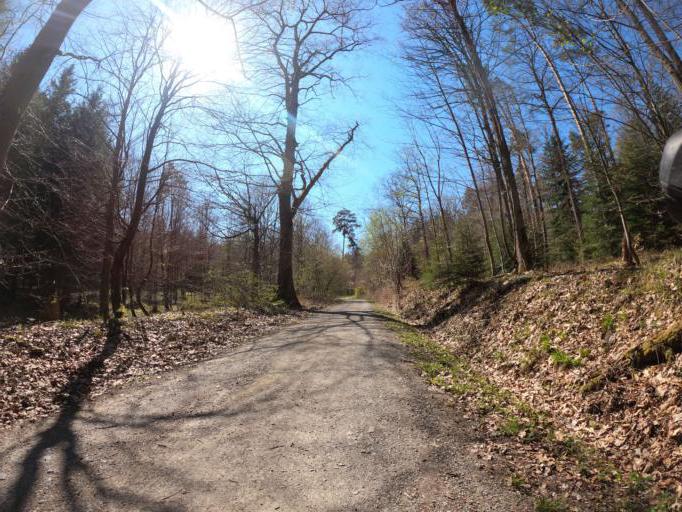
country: DE
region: Baden-Wuerttemberg
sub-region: Karlsruhe Region
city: Niefern-Oschelbronn
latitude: 48.8993
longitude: 8.7892
